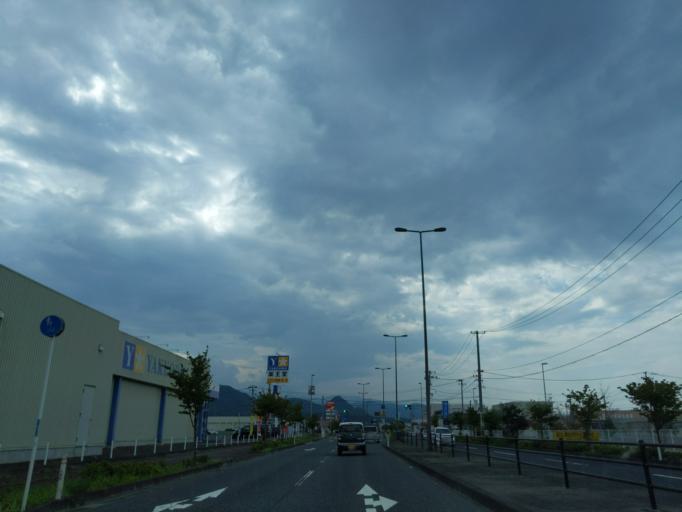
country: JP
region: Miyagi
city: Tomiya
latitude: 38.4365
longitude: 140.8861
